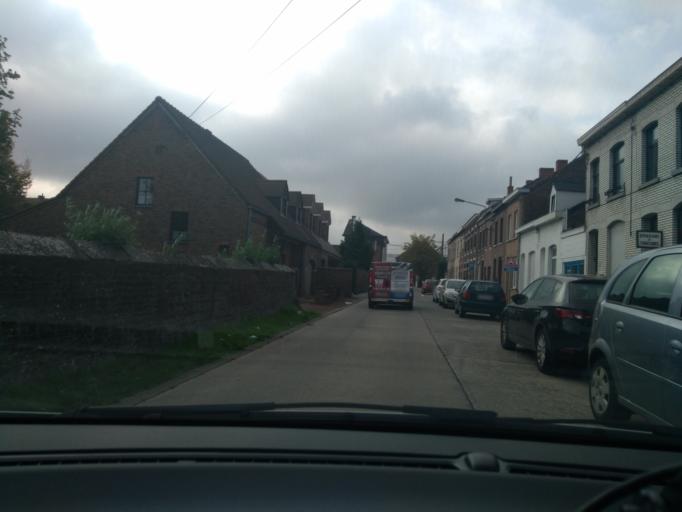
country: BE
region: Wallonia
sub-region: Province du Hainaut
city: Frameries
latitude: 50.4121
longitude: 3.8884
